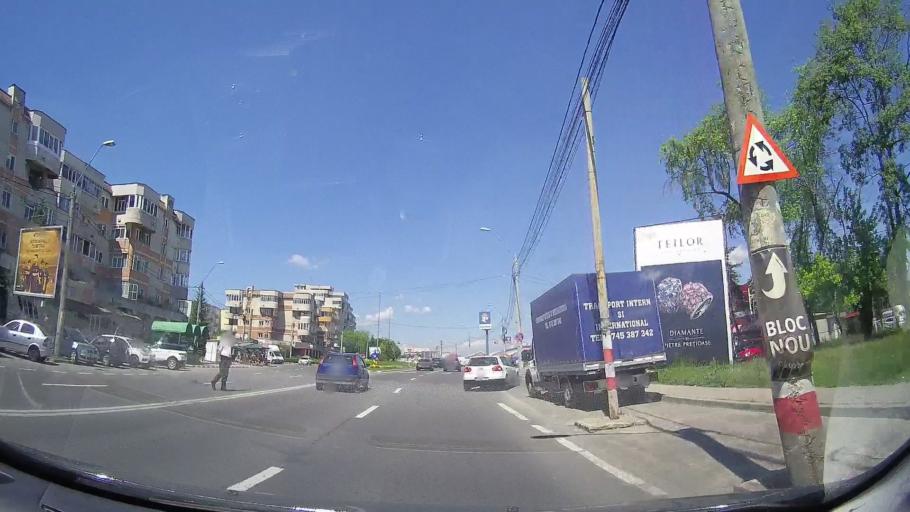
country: RO
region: Arges
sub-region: Comuna Bascov
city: Bascov
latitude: 44.8784
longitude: 24.8416
